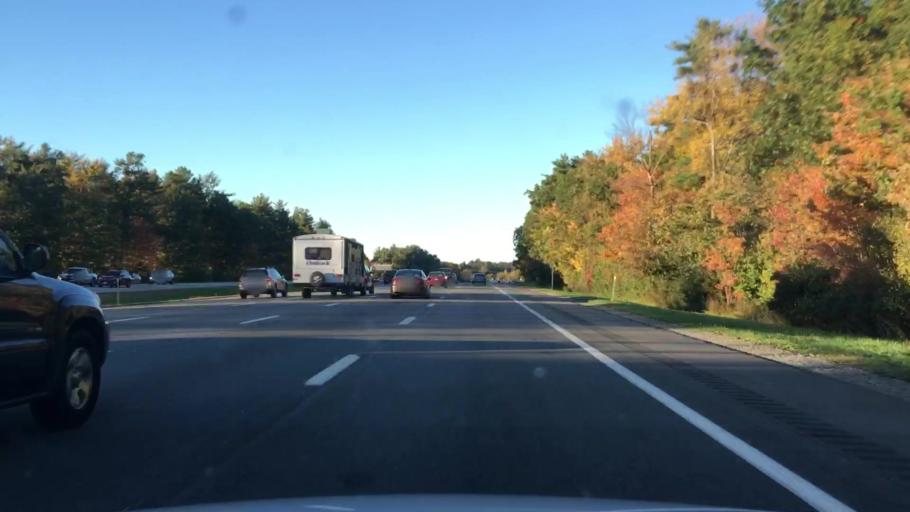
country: US
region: New Hampshire
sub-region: Rockingham County
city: North Hampton
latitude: 42.9846
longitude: -70.8516
